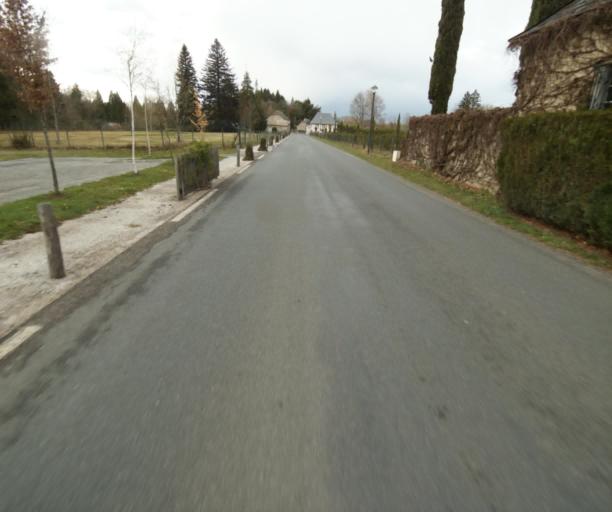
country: FR
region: Limousin
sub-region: Departement de la Correze
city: Saint-Privat
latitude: 45.2177
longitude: 2.0041
